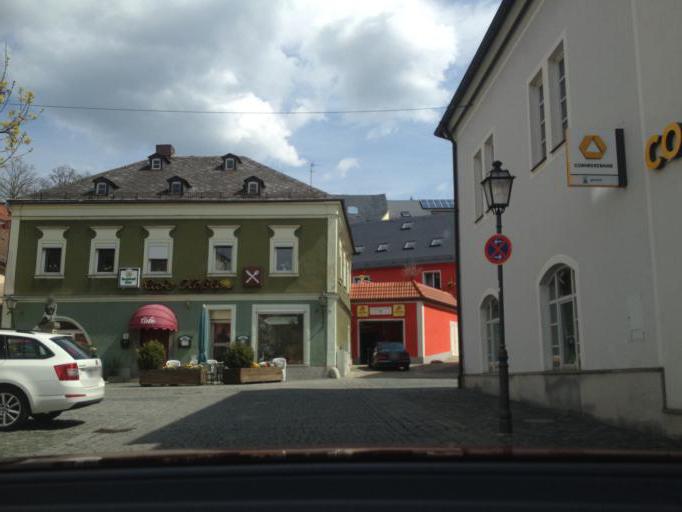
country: DE
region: Bavaria
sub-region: Upper Franconia
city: Arzberg
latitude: 50.0575
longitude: 12.1861
